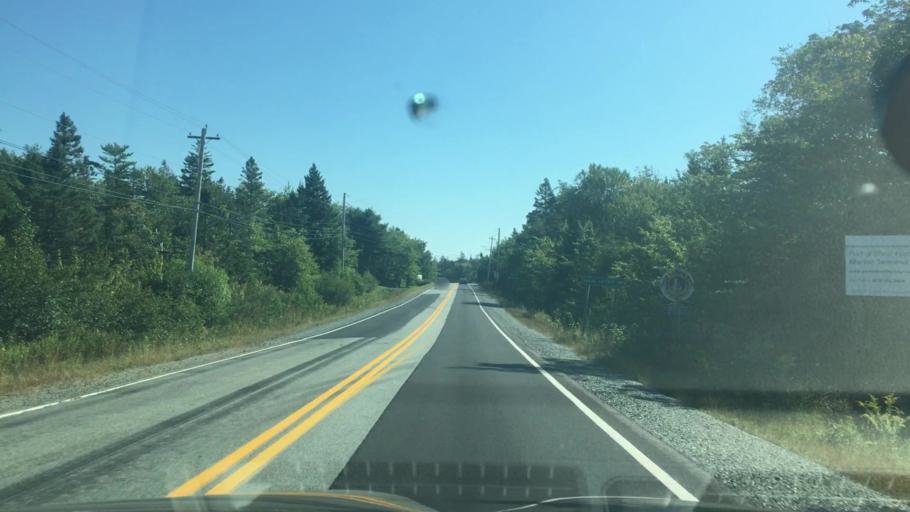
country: CA
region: Nova Scotia
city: New Glasgow
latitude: 44.9103
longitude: -62.5488
